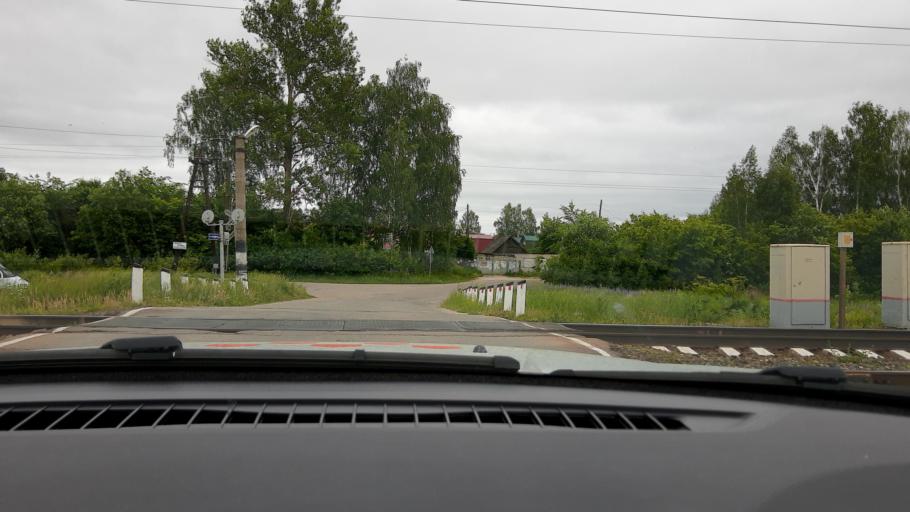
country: RU
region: Nizjnij Novgorod
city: Sitniki
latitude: 56.5200
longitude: 44.0493
